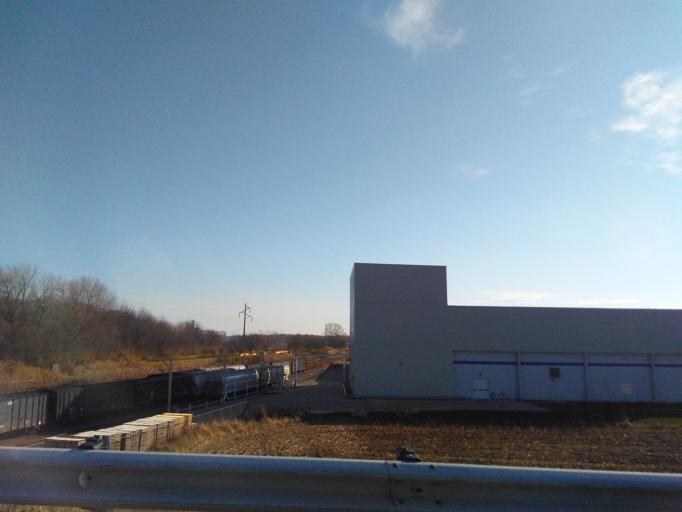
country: US
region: Illinois
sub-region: Bond County
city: Greenville
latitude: 38.8838
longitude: -89.3908
